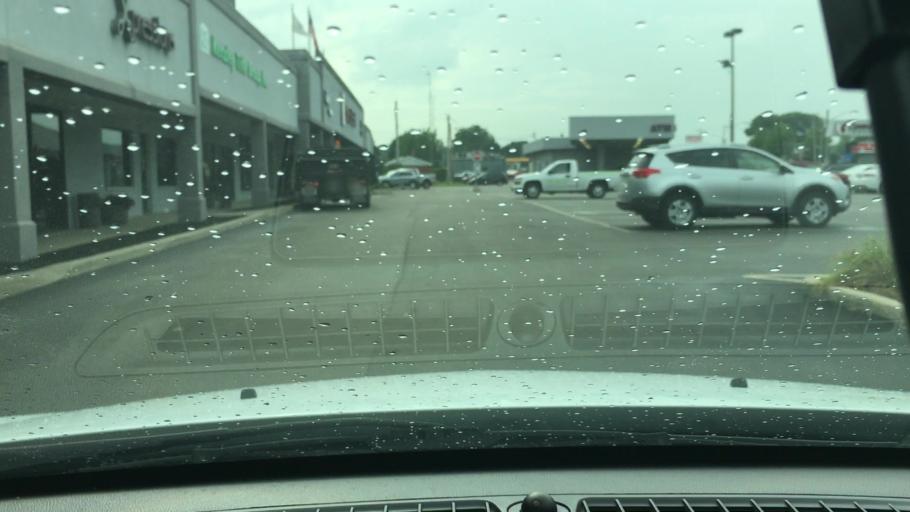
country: US
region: Illinois
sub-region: Ogle County
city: Rochelle
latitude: 41.9335
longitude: -89.0640
